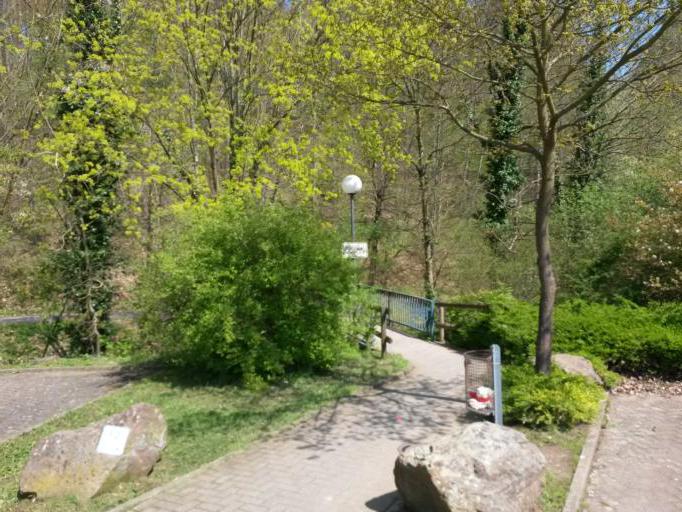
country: DE
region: Baden-Wuerttemberg
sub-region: Karlsruhe Region
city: Konigsbach-Stein
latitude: 48.9682
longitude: 8.5571
